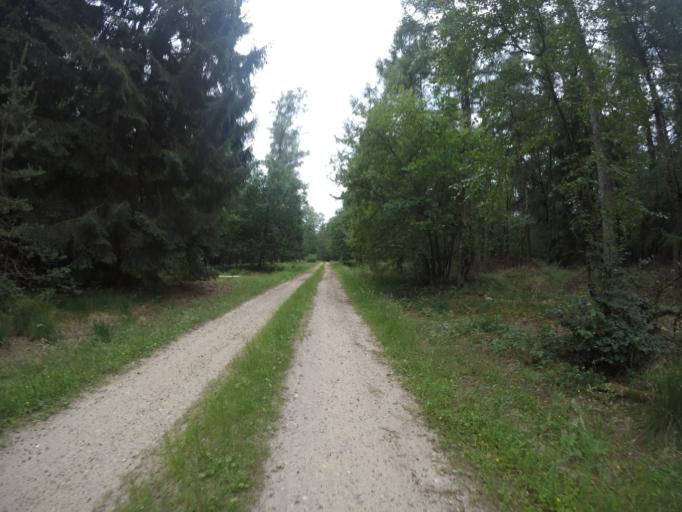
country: DE
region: Lower Saxony
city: Undeloh
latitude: 53.2138
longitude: 9.9766
